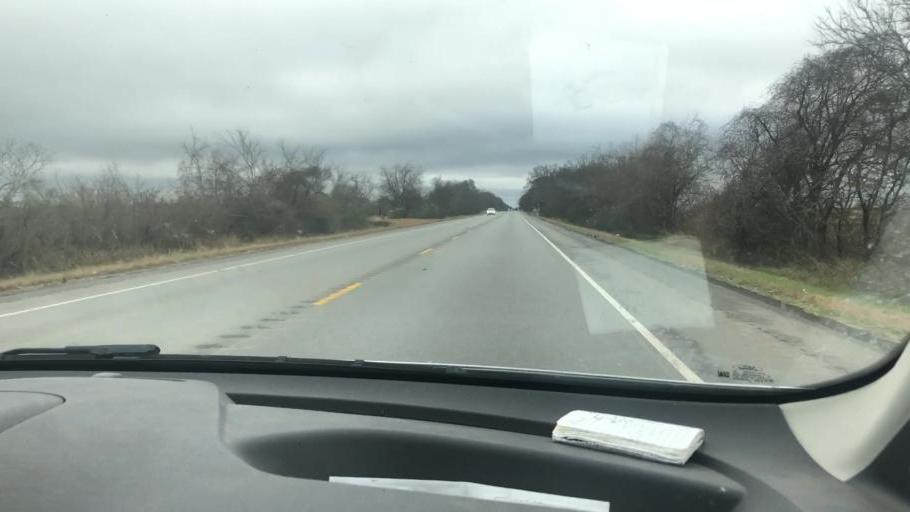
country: US
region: Texas
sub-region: Matagorda County
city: Bay City
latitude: 29.1128
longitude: -95.9795
